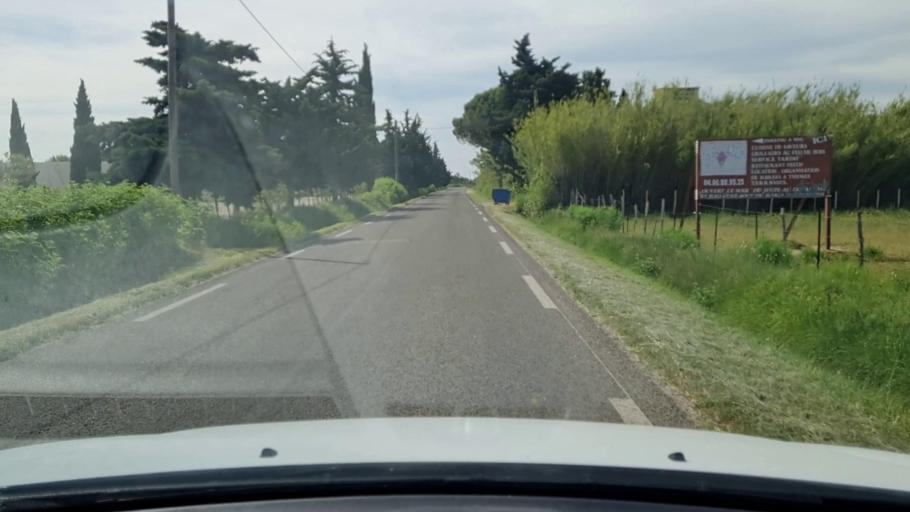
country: FR
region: Languedoc-Roussillon
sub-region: Departement du Gard
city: Aigues-Mortes
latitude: 43.6181
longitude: 4.2048
